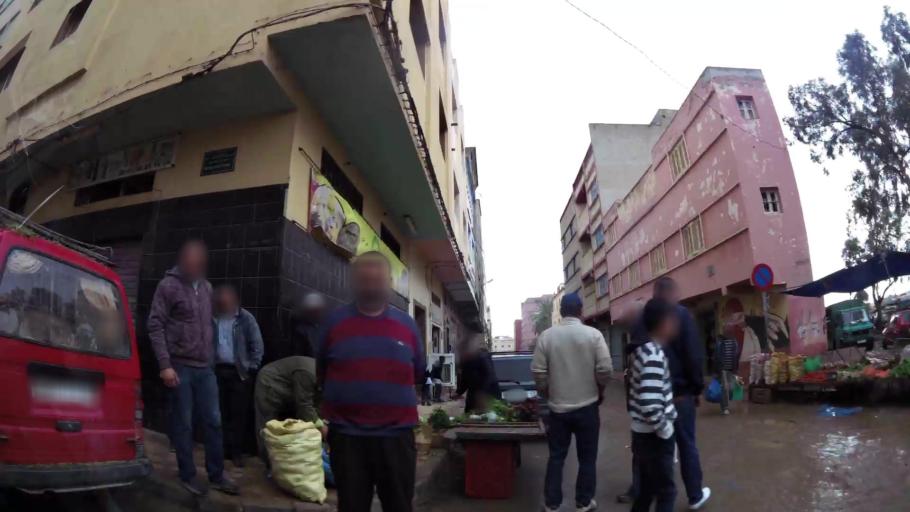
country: MA
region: Oriental
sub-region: Nador
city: Nador
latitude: 35.1524
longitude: -3.0056
